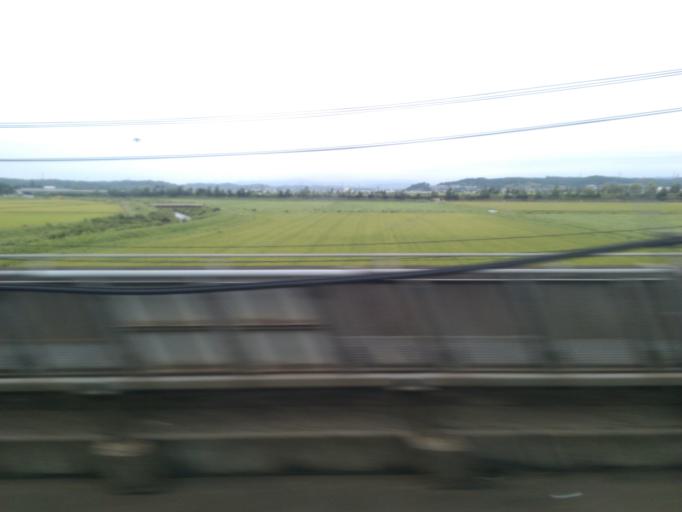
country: JP
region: Iwate
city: Ichinoseki
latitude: 38.7981
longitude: 141.0956
